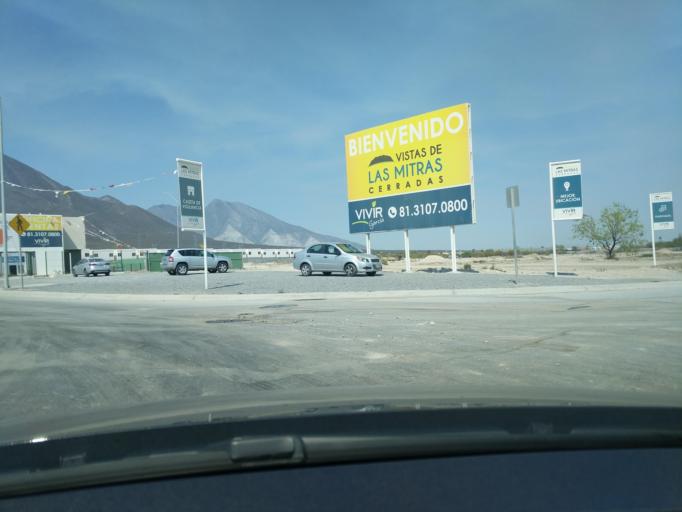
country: MX
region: Nuevo Leon
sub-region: Garcia
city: Valle de Lincoln
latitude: 25.7937
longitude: -100.4709
